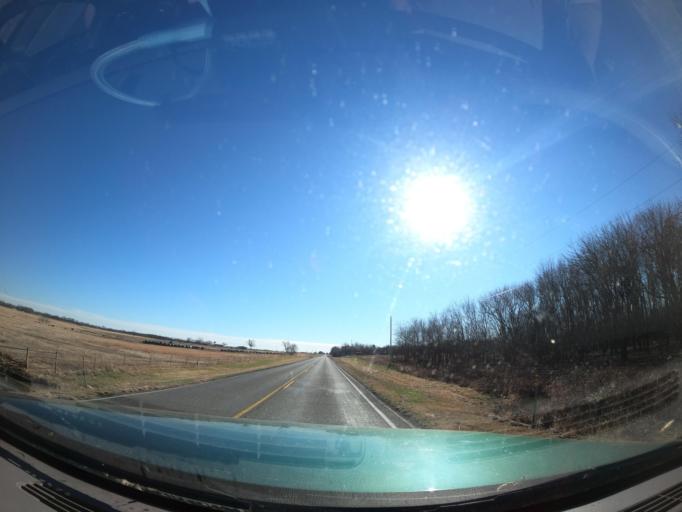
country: US
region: Oklahoma
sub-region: Muskogee County
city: Haskell
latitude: 35.6797
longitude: -95.6422
